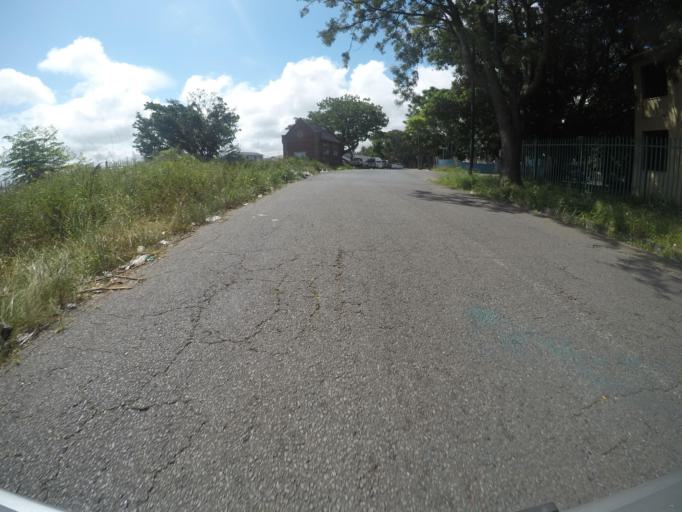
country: ZA
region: Eastern Cape
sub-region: Buffalo City Metropolitan Municipality
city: East London
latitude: -33.0029
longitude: 27.8959
